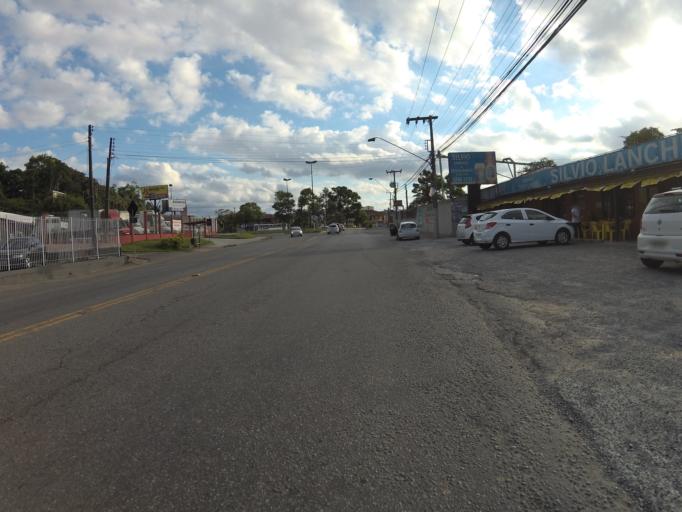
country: BR
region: Santa Catarina
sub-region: Blumenau
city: Blumenau
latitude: -26.8699
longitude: -49.0926
